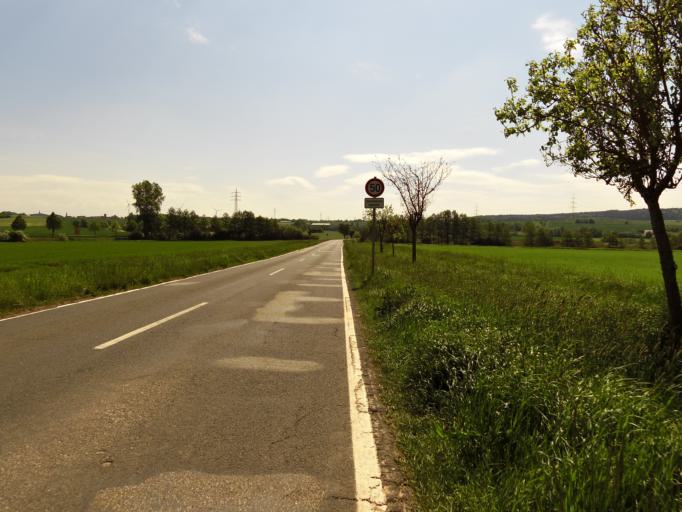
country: DE
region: Rheinland-Pfalz
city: Dreisen
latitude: 49.5969
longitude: 8.0221
